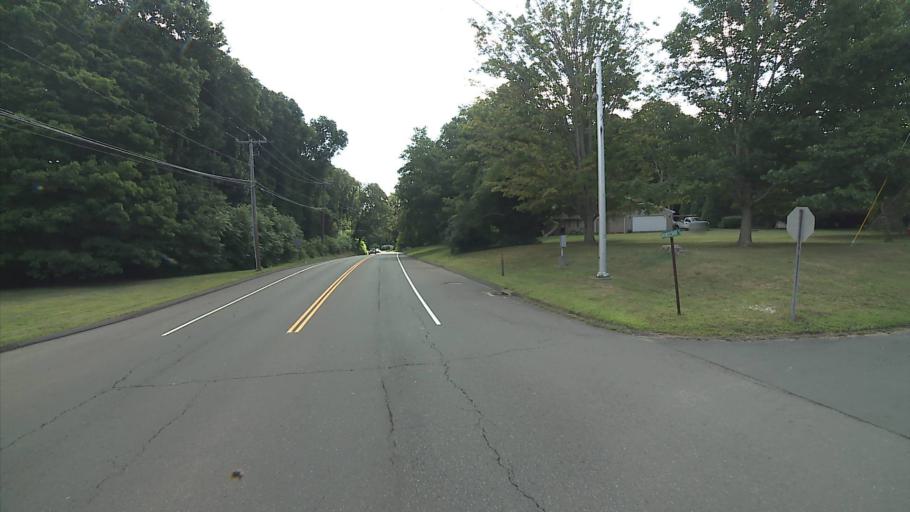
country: US
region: Connecticut
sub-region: New Haven County
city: Guilford Center
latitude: 41.2866
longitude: -72.6531
